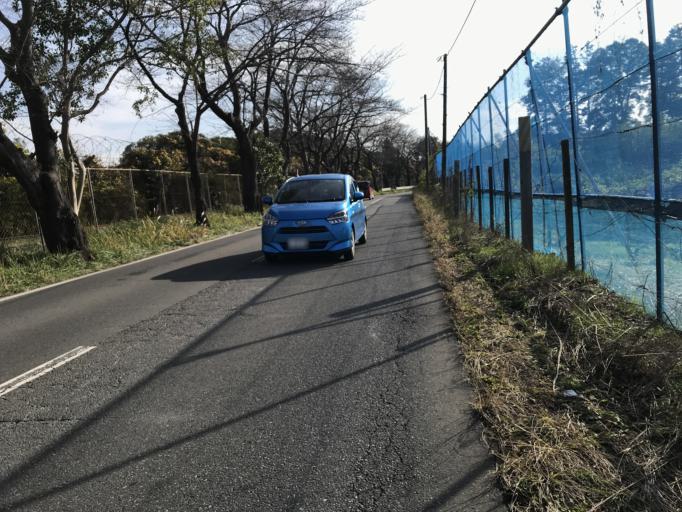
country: JP
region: Chiba
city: Shiroi
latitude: 35.7885
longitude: 140.0103
